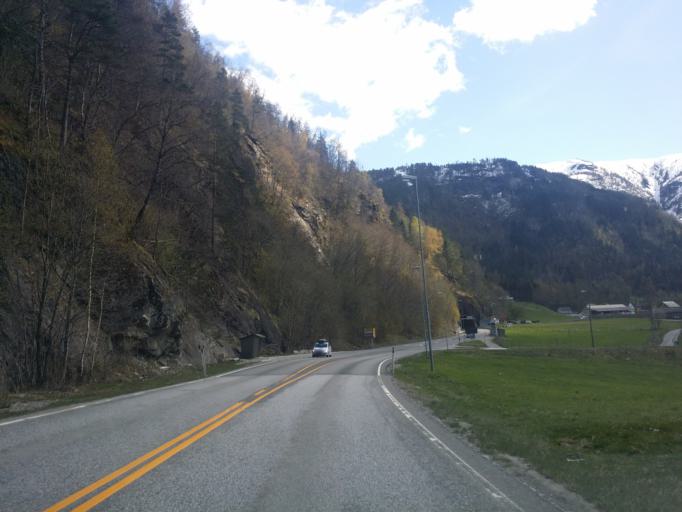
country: NO
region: Hordaland
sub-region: Granvin
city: Granvin
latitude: 60.5357
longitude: 6.7332
